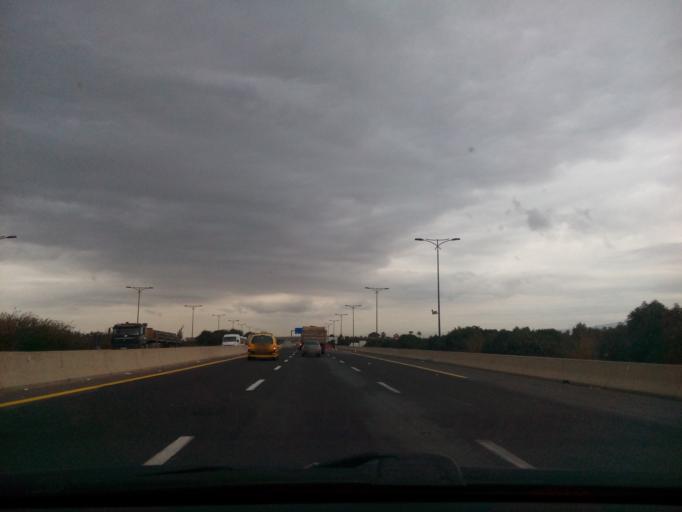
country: DZ
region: Mascara
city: Sig
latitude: 35.5816
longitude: -0.2273
